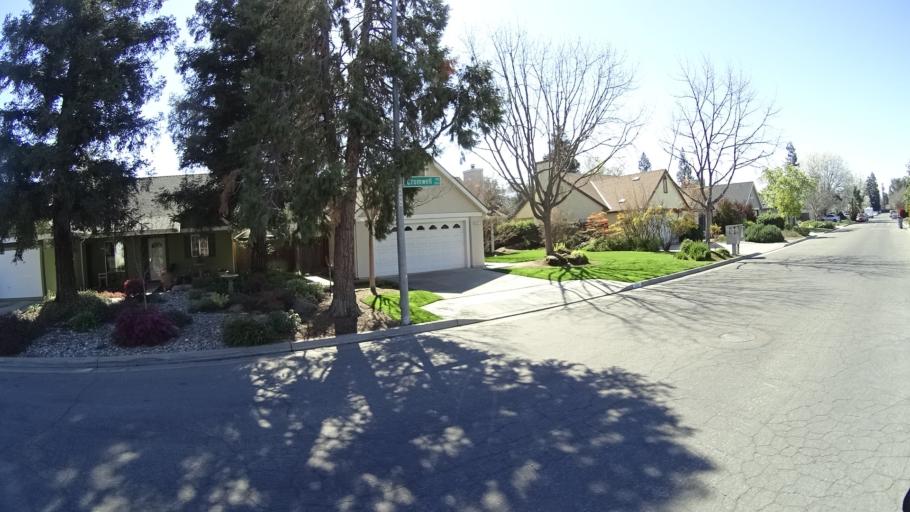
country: US
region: California
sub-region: Fresno County
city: Clovis
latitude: 36.8473
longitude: -119.7436
